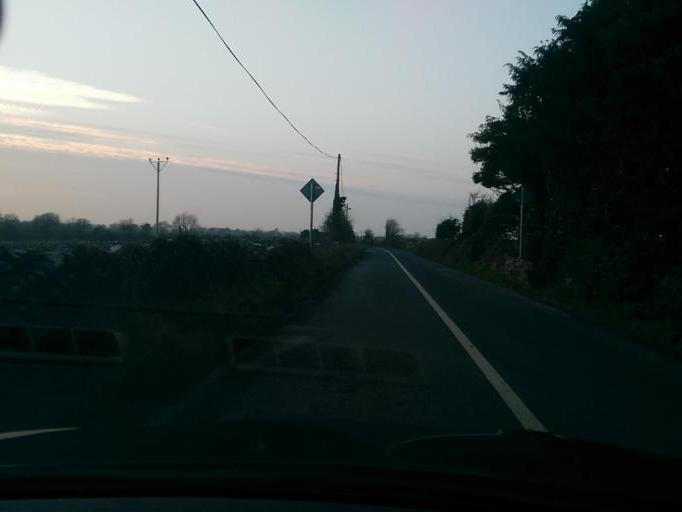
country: IE
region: Connaught
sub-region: County Galway
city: Athenry
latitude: 53.2451
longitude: -8.6598
